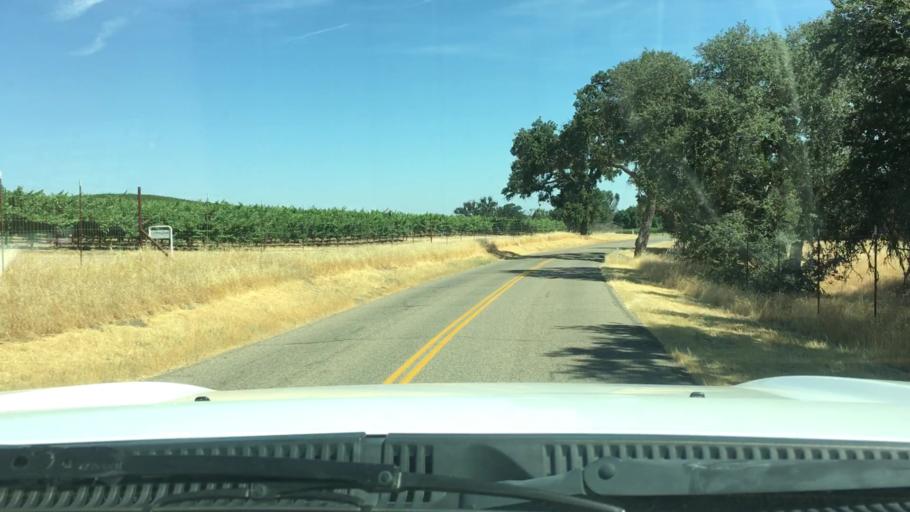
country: US
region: California
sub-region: San Luis Obispo County
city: Templeton
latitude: 35.5674
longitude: -120.6073
